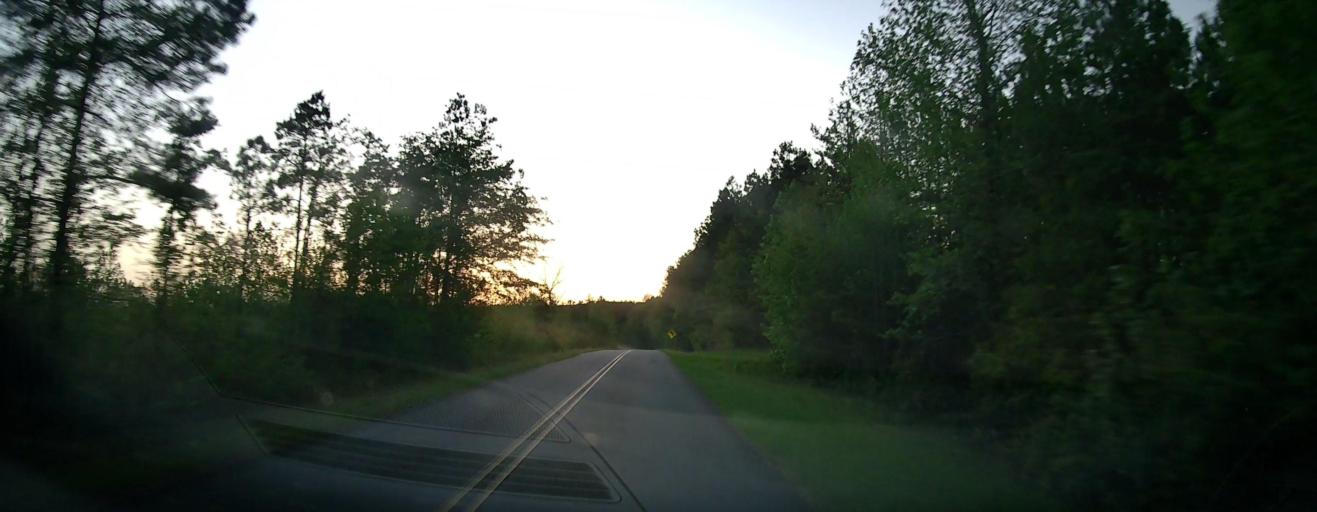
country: US
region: Georgia
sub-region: Marion County
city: Buena Vista
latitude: 32.2558
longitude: -84.5887
